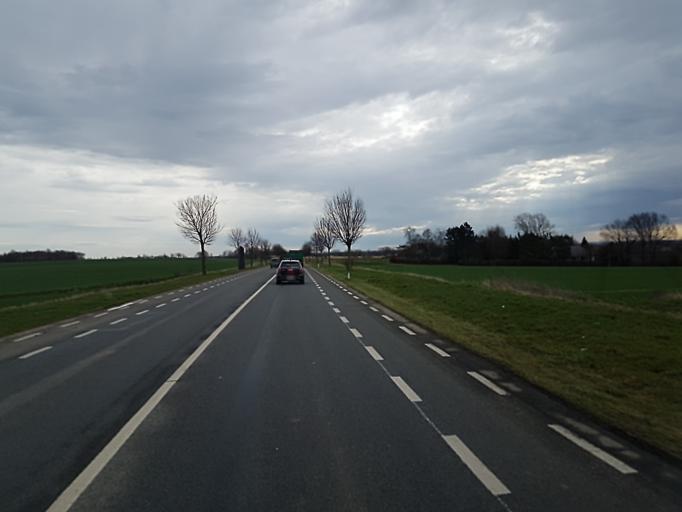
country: BE
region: Wallonia
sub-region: Province de Liege
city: Oreye
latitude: 50.7360
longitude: 5.3560
